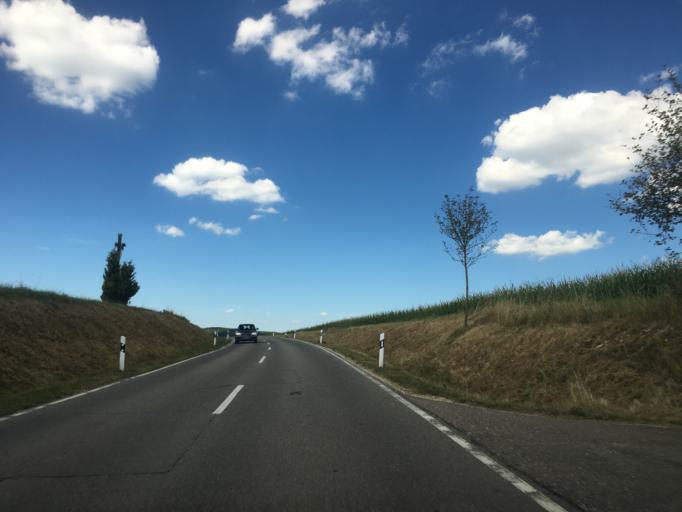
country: DE
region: Baden-Wuerttemberg
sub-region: Tuebingen Region
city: Hayingen
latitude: 48.3148
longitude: 9.4444
